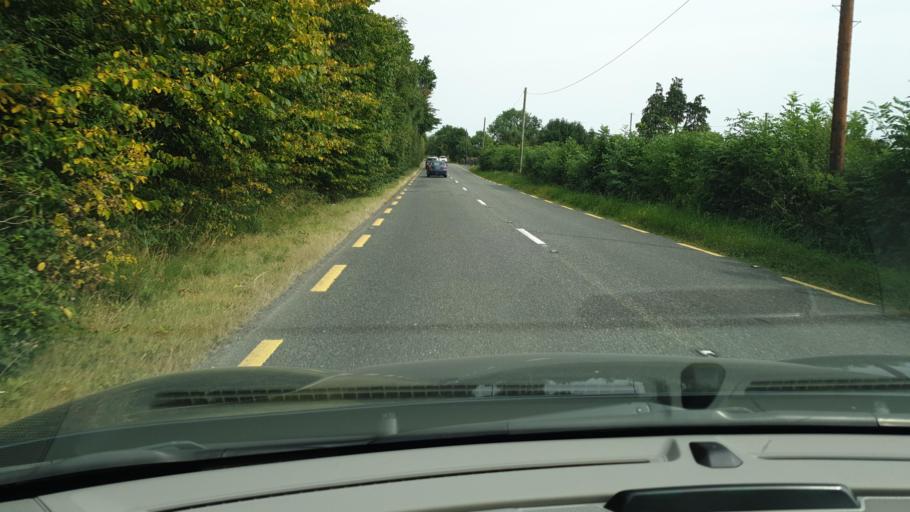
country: IE
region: Leinster
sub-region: An Mhi
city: Athboy
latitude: 53.6797
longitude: -6.9528
